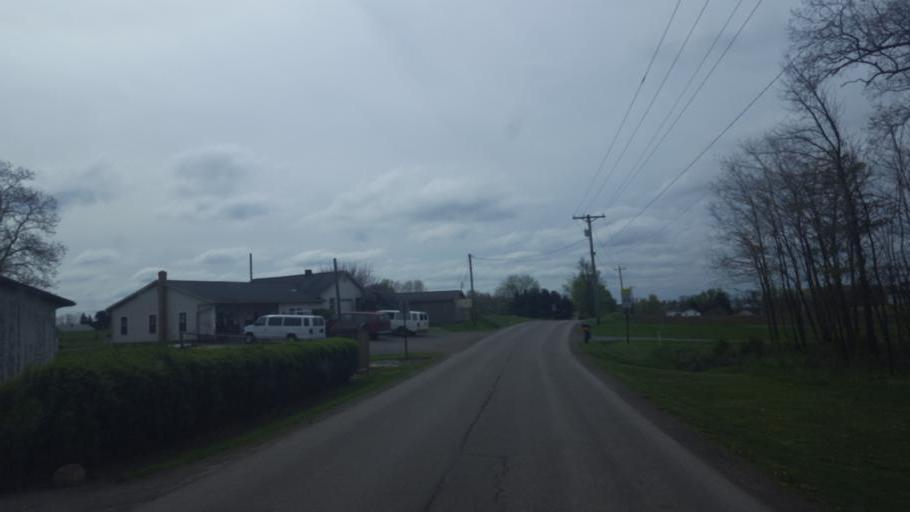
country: US
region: Ohio
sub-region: Wayne County
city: Apple Creek
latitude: 40.6969
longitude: -81.8216
